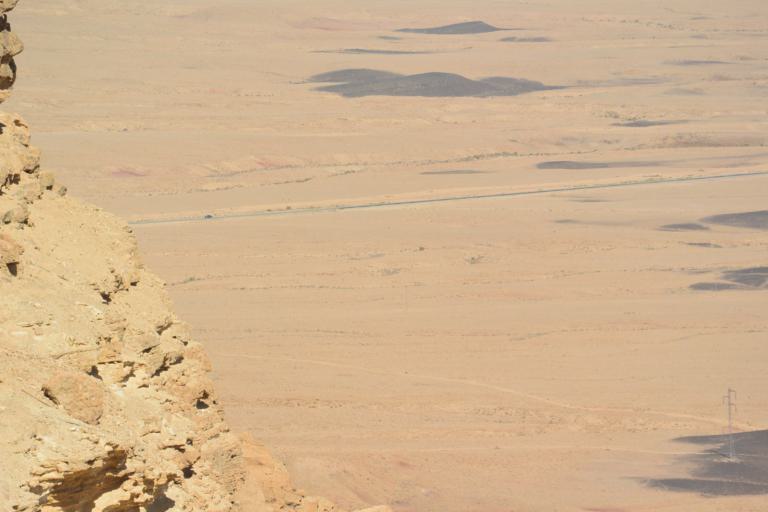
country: IL
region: Southern District
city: Mitzpe Ramon
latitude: 30.6065
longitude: 34.8042
